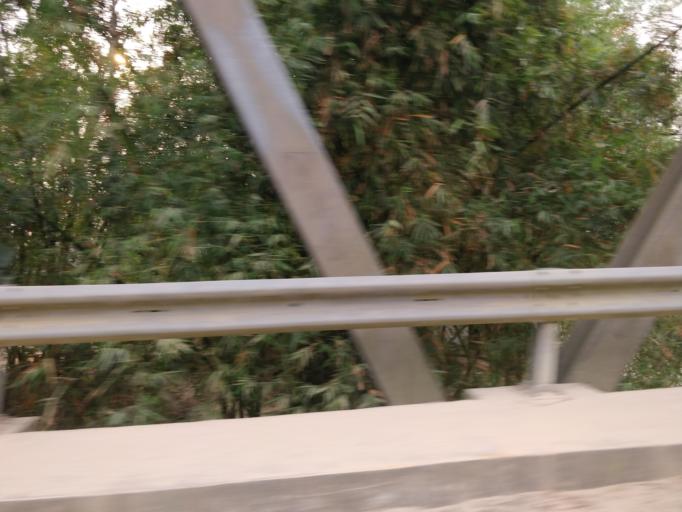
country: BD
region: Sylhet
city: Habiganj
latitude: 24.1457
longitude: 91.3513
